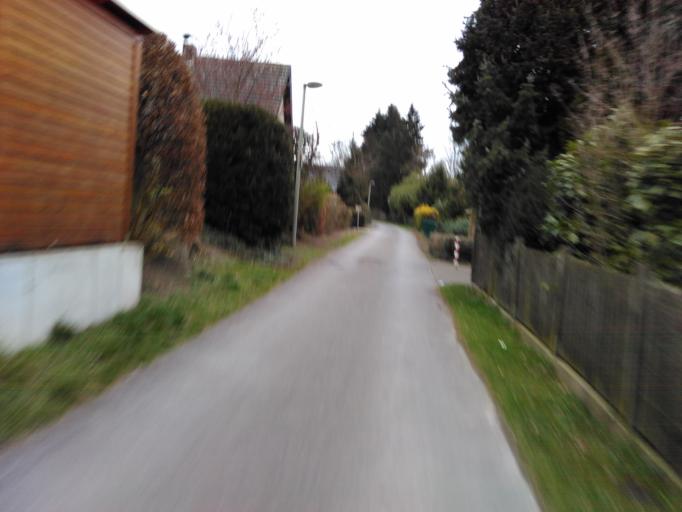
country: DE
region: North Rhine-Westphalia
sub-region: Regierungsbezirk Detmold
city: Verl
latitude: 51.8769
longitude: 8.5018
